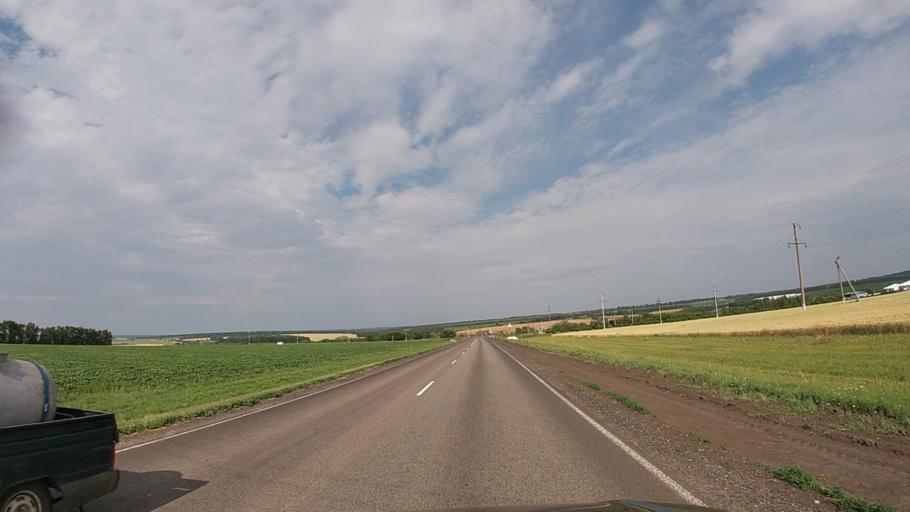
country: RU
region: Belgorod
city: Krasnaya Yaruga
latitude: 50.7981
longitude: 35.5833
